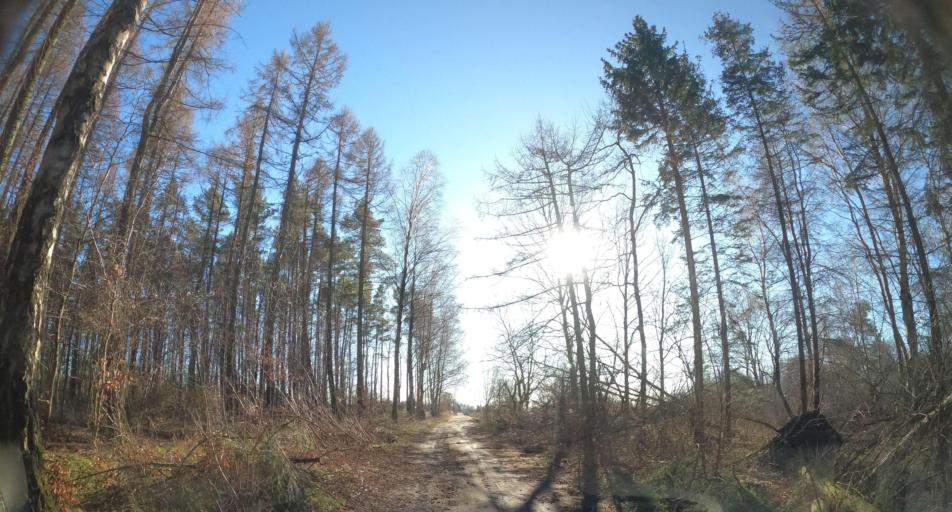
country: PL
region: West Pomeranian Voivodeship
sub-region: Powiat kamienski
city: Dziwnow
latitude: 54.0344
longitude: 14.8372
